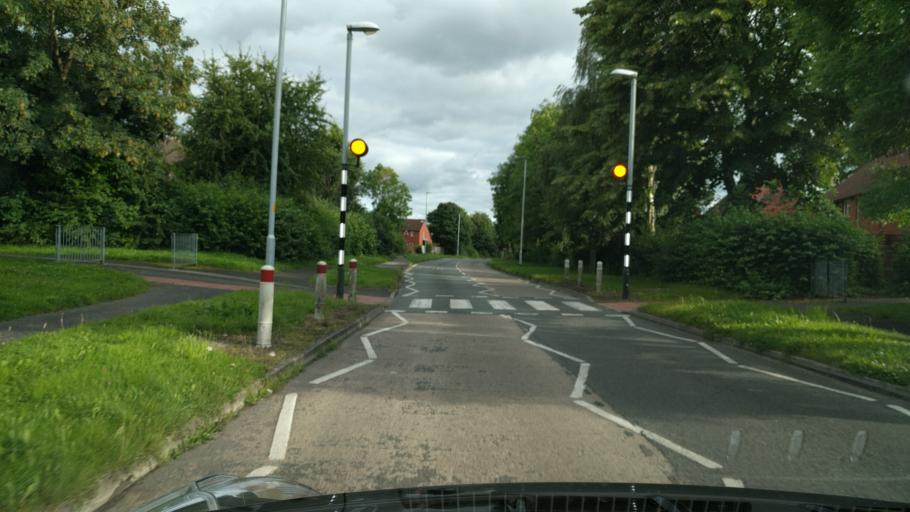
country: GB
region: England
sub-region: Warrington
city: Croft
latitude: 53.4191
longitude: -2.5564
